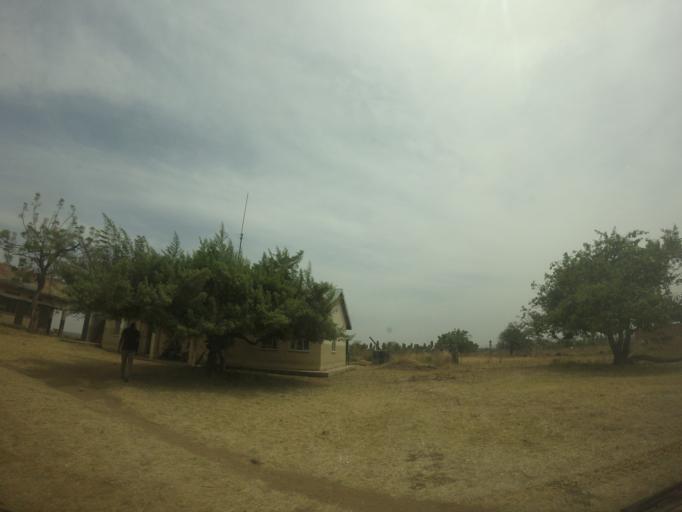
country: UG
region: Northern Region
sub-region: Nebbi District
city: Nebbi
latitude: 2.6367
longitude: 31.0298
